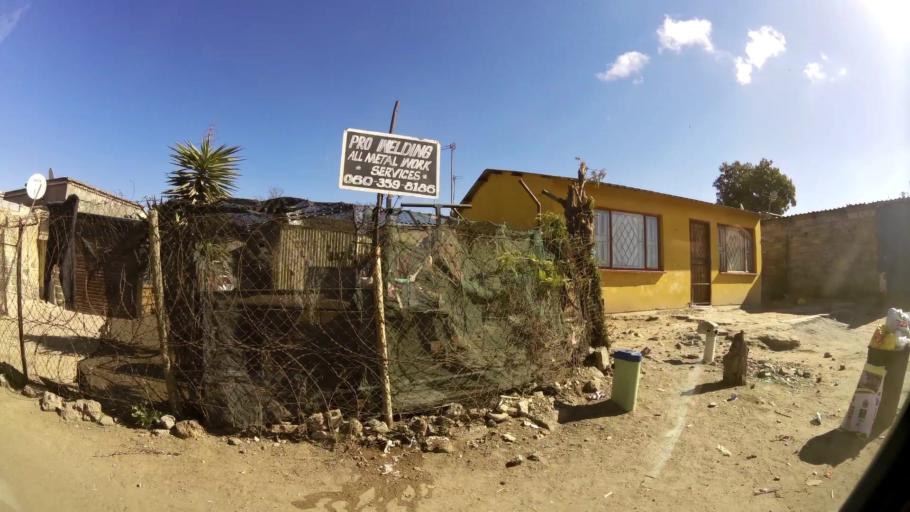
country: ZA
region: Gauteng
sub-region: Ekurhuleni Metropolitan Municipality
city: Tembisa
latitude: -26.0343
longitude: 28.1877
